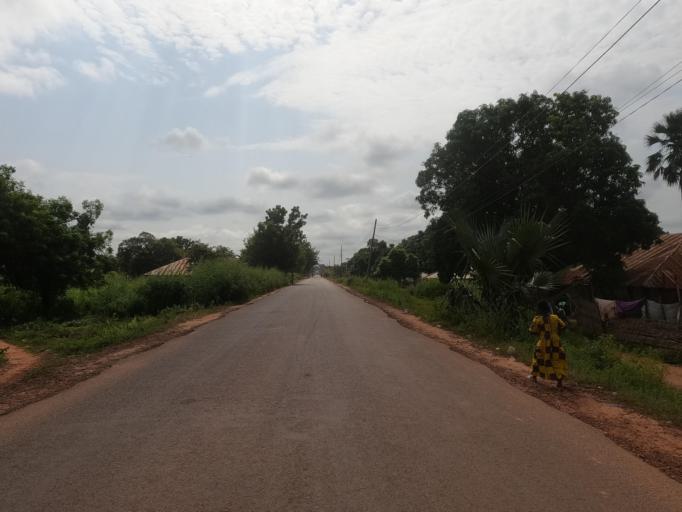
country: SN
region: Ziguinchor
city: Adeane
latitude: 12.4031
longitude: -15.7932
